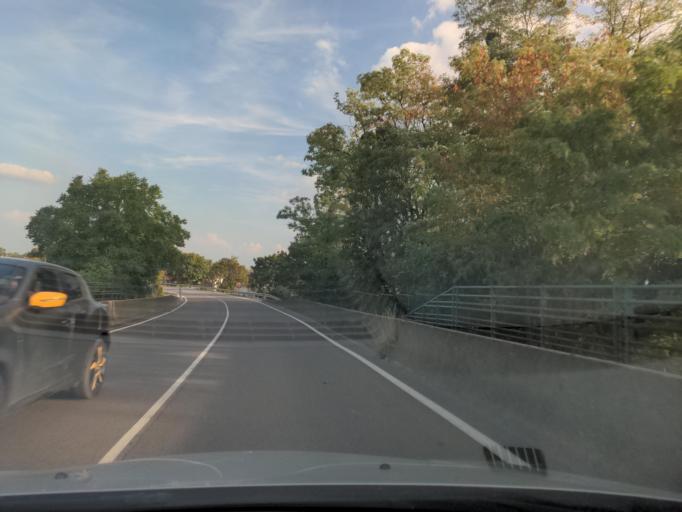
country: FR
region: Bourgogne
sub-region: Departement de la Cote-d'Or
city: Sennecey-les-Dijon
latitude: 47.2848
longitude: 5.0997
